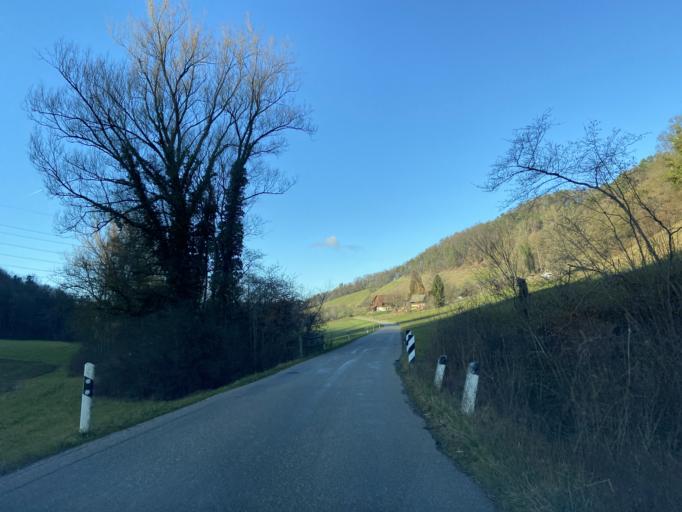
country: CH
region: Zurich
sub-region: Bezirk Winterthur
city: Wuelflingen (Kreis 6) / Niederfeld
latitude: 47.5008
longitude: 8.6622
